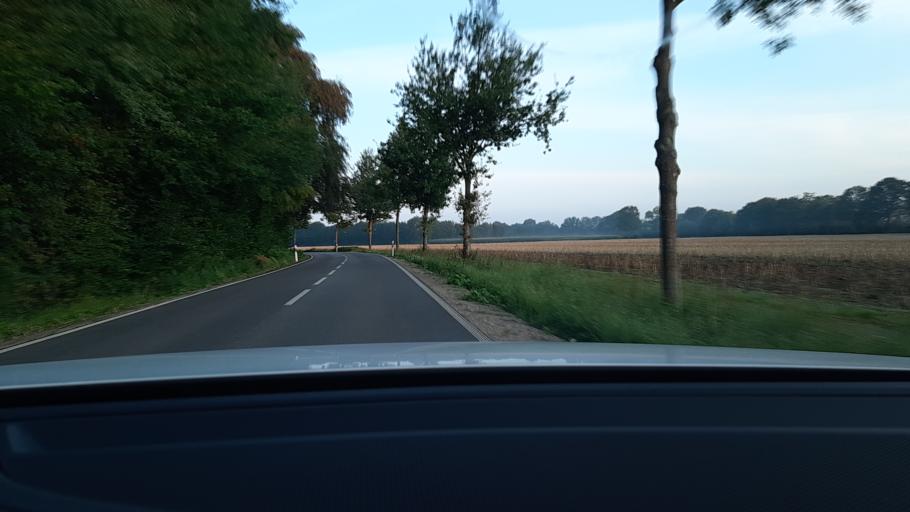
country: DE
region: Schleswig-Holstein
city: Hamberge
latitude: 53.8203
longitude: 10.5858
